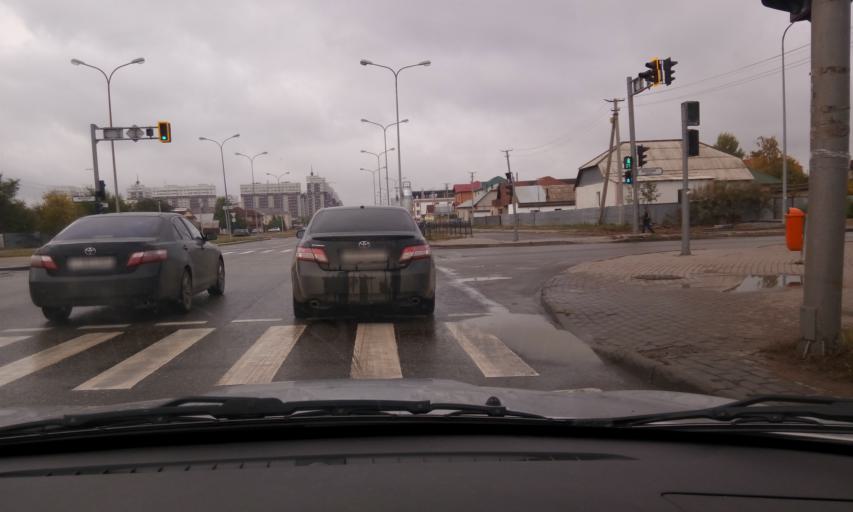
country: KZ
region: Astana Qalasy
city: Astana
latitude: 51.1364
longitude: 71.5131
